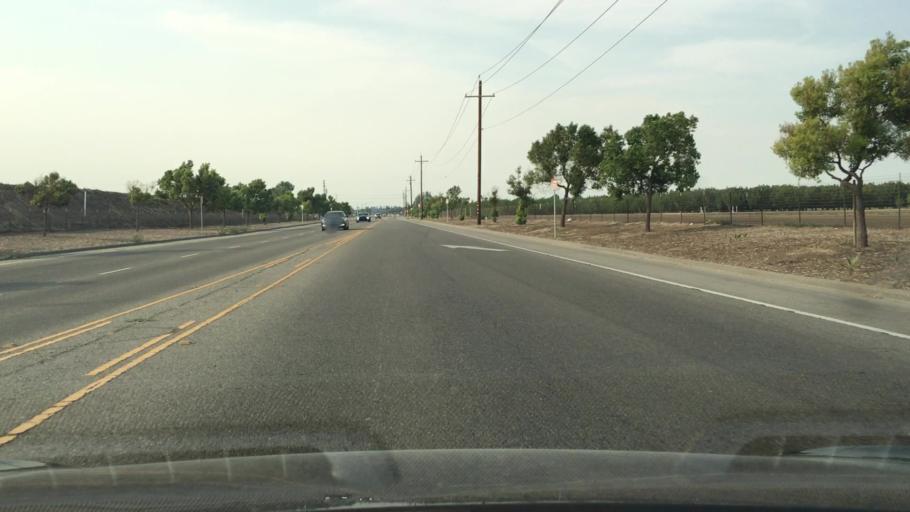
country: US
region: California
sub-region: Fresno County
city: Clovis
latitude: 36.8171
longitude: -119.7361
